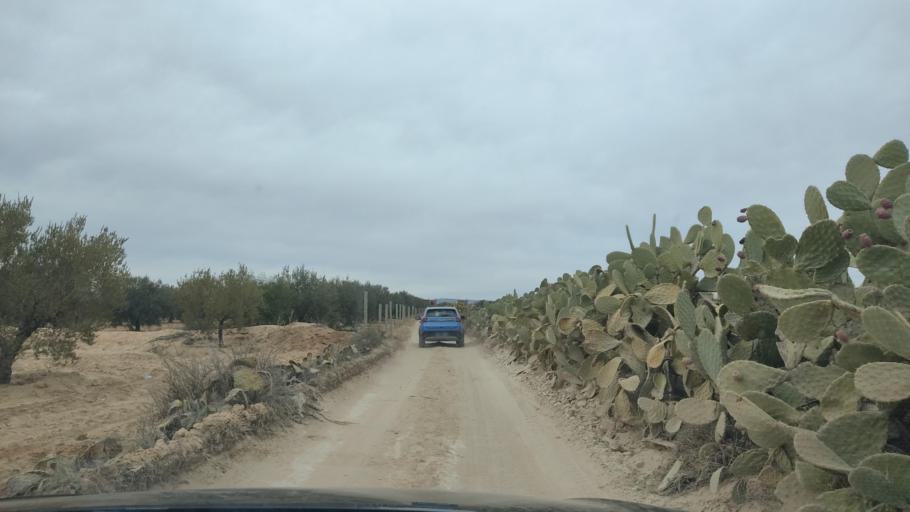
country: TN
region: Al Qasrayn
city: Kasserine
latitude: 35.2277
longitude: 8.9153
